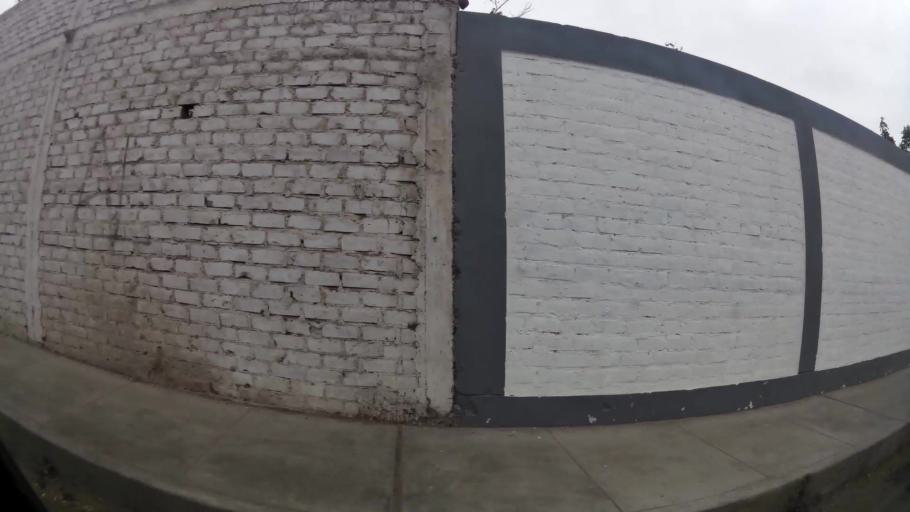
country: PE
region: La Libertad
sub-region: Provincia de Trujillo
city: Trujillo
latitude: -8.1252
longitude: -79.0287
